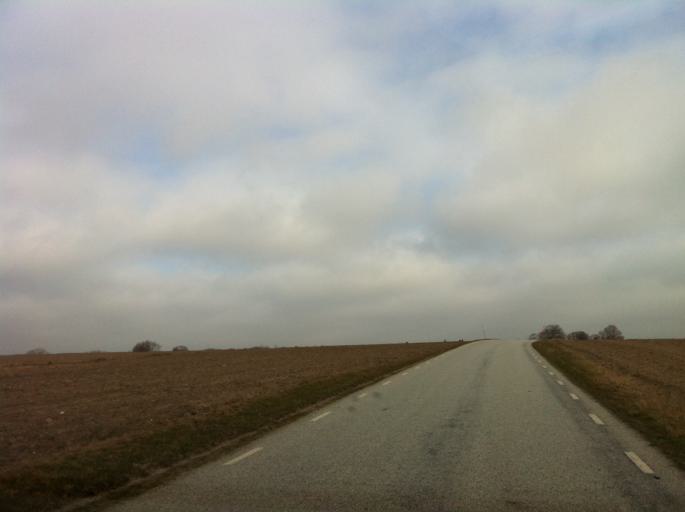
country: SE
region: Skane
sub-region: Kavlinge Kommun
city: Kaevlinge
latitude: 55.8159
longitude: 13.0912
